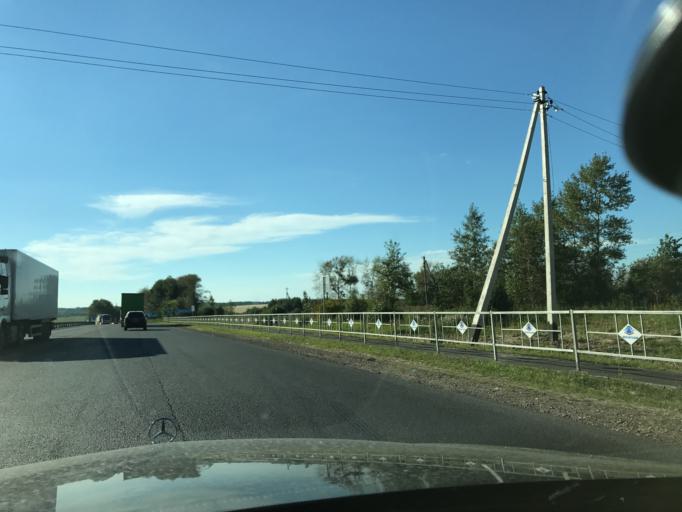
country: RU
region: Vladimir
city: Novovyazniki
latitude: 56.2140
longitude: 42.2571
